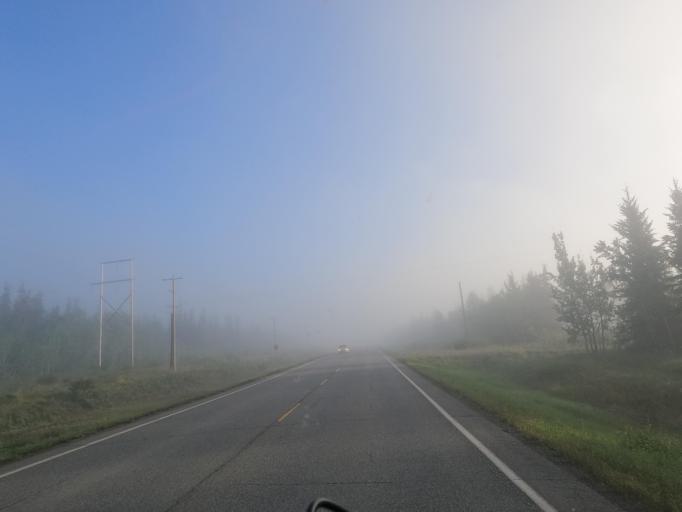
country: CA
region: Yukon
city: Whitehorse
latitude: 60.8888
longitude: -135.1837
